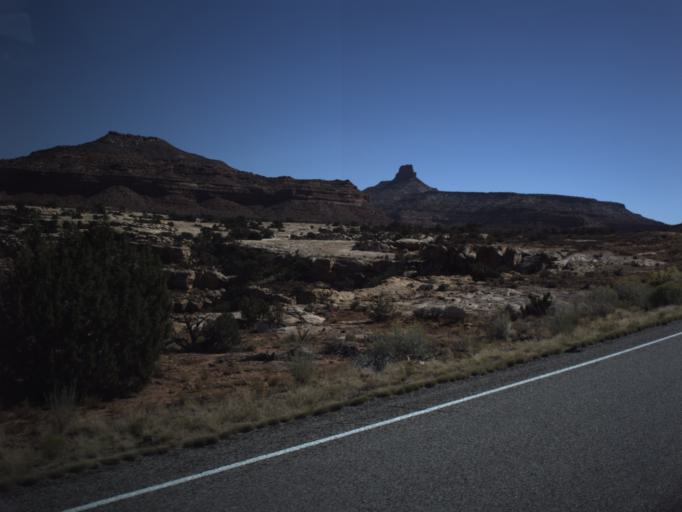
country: US
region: Utah
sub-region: San Juan County
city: Blanding
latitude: 37.7369
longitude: -110.2723
